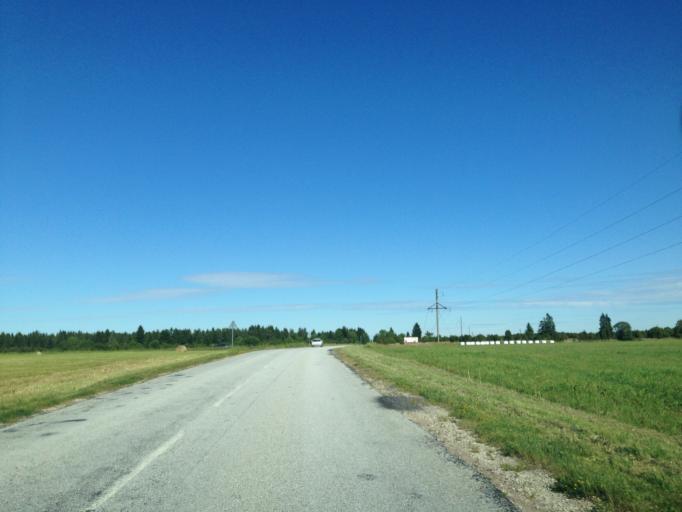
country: EE
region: Harju
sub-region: Raasiku vald
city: Raasiku
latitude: 59.4684
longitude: 25.2610
